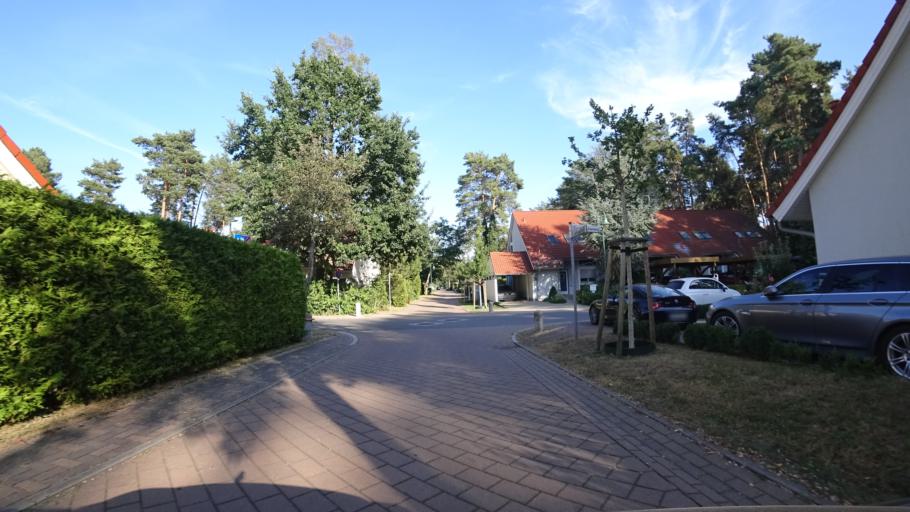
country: DE
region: Brandenburg
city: Stahnsdorf
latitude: 52.3988
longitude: 13.1998
